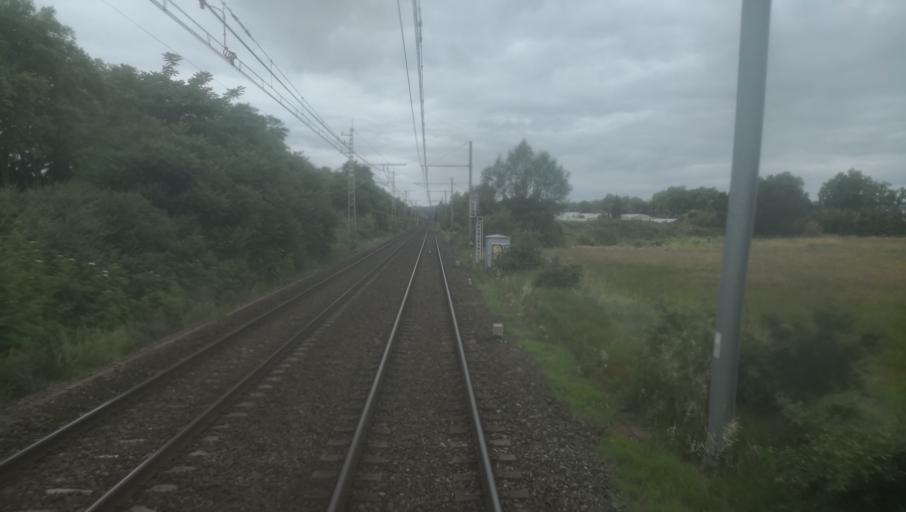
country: FR
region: Midi-Pyrenees
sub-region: Departement de la Haute-Garonne
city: Saint-Jory
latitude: 43.7495
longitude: 1.3636
